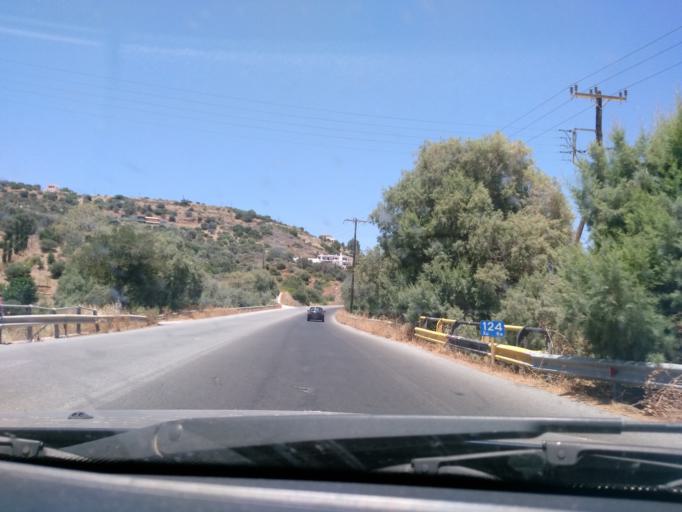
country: GR
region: Crete
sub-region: Nomos Irakleiou
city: Gazi
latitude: 35.3588
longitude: 25.0390
